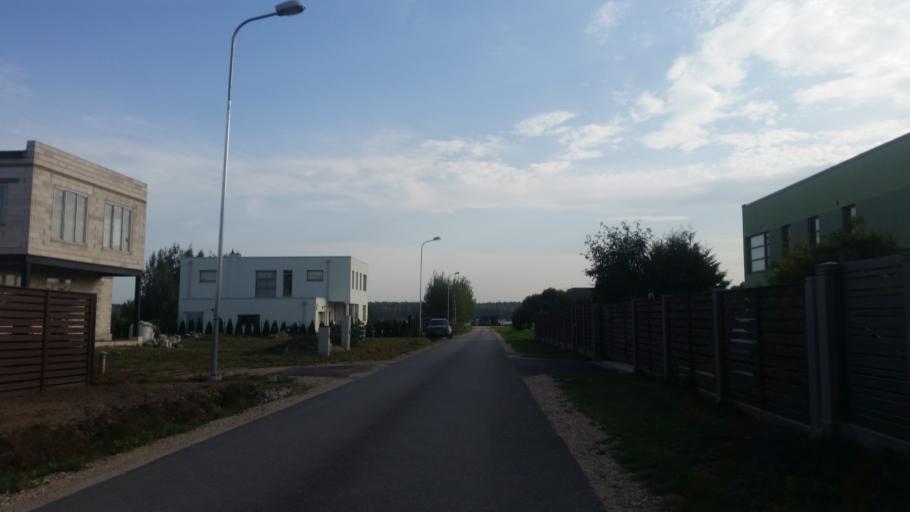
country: LV
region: Ikskile
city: Ikskile
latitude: 56.8184
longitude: 24.5114
